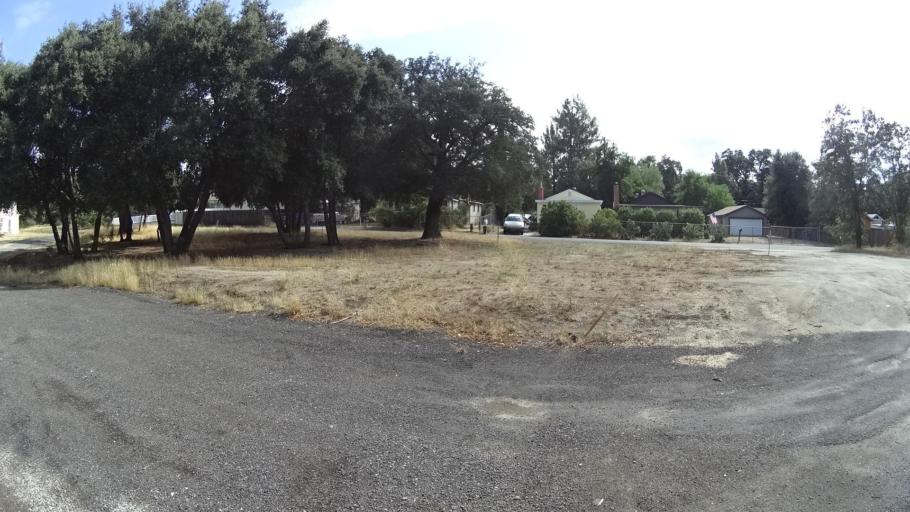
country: US
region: California
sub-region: San Diego County
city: Campo
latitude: 32.6819
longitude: -116.5115
